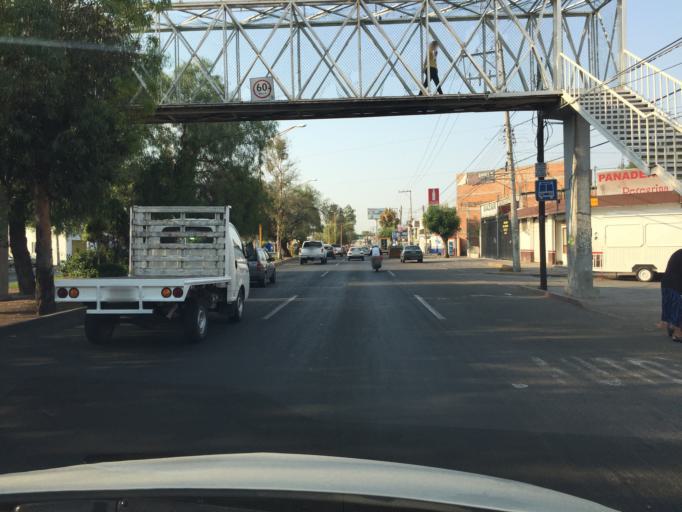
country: MX
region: Aguascalientes
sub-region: Aguascalientes
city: La Loma de los Negritos
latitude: 21.8647
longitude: -102.3177
